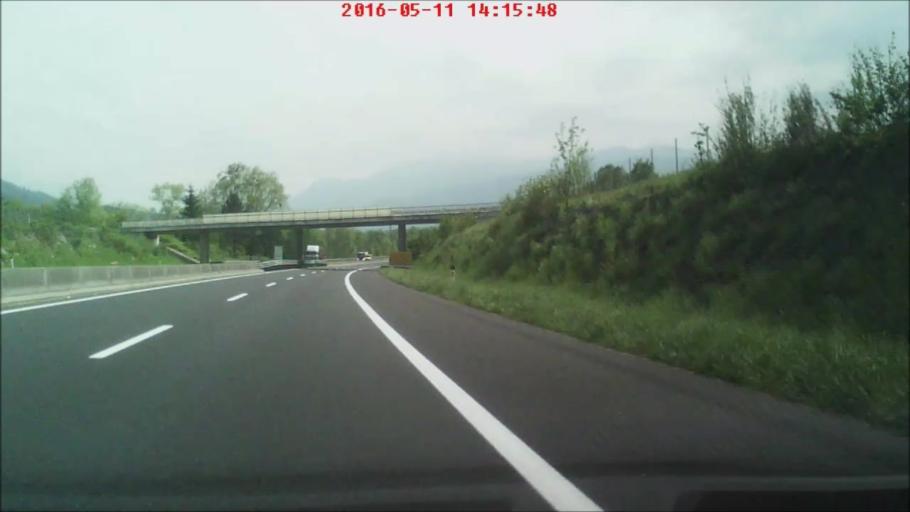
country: AT
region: Upper Austria
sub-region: Politischer Bezirk Kirchdorf an der Krems
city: Micheldorf in Oberoesterreich
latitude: 47.9556
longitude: 14.1009
